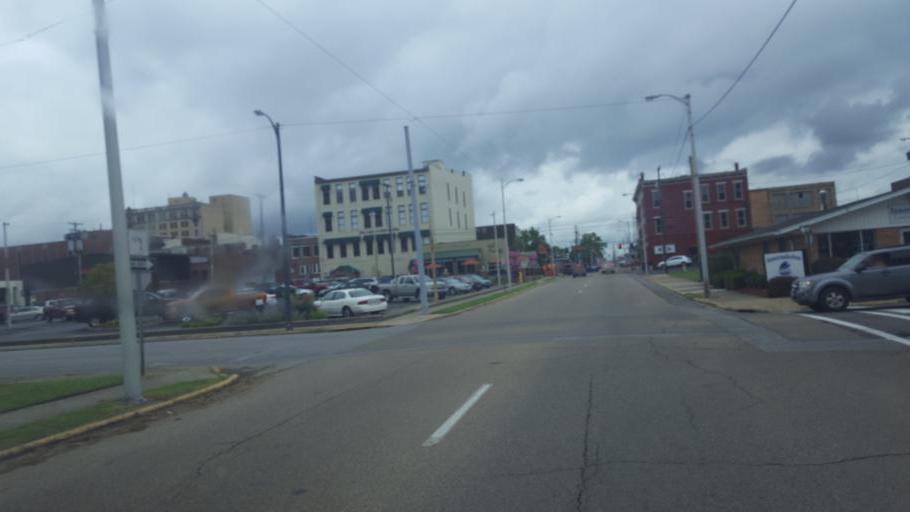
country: US
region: Ohio
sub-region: Scioto County
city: Portsmouth
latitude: 38.7330
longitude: -82.9946
